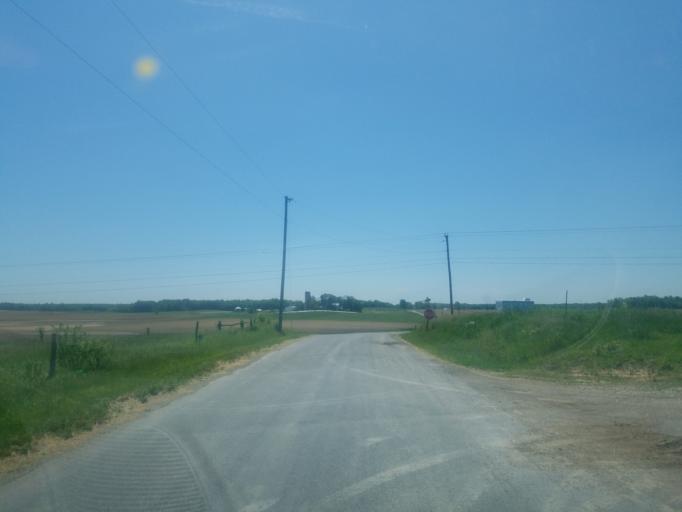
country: US
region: Ohio
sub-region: Huron County
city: Greenwich
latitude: 40.9934
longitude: -82.4567
